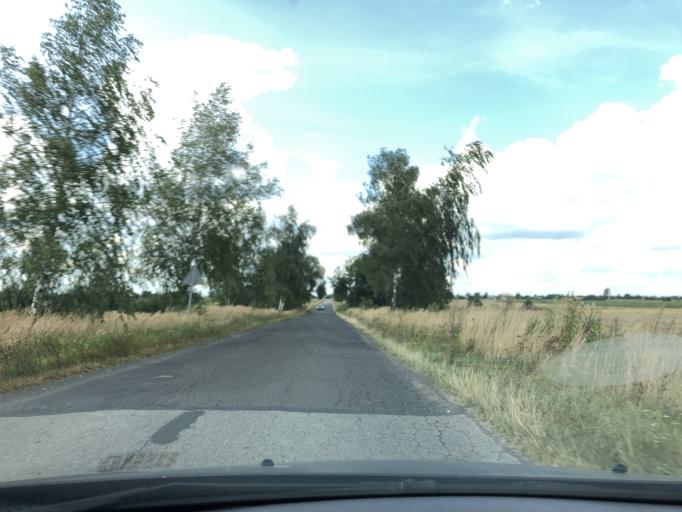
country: PL
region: Lodz Voivodeship
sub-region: Powiat wieruszowski
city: Walichnowy
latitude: 51.2482
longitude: 18.3894
